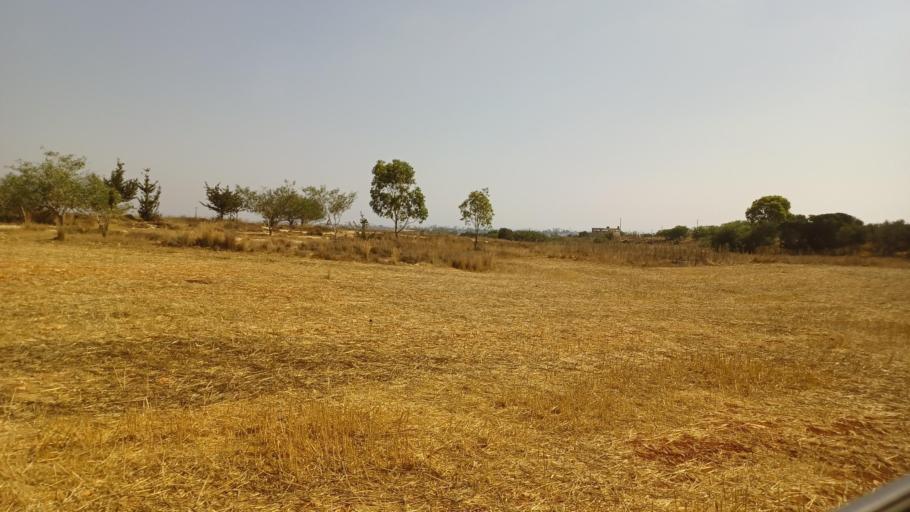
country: CY
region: Ammochostos
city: Deryneia
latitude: 35.0699
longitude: 33.9509
